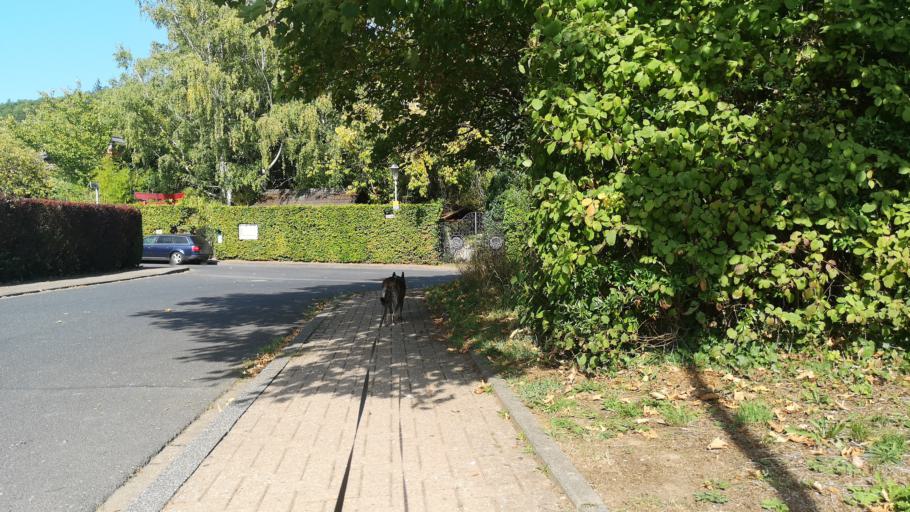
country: DE
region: North Rhine-Westphalia
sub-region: Regierungsbezirk Koln
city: Nideggen
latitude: 50.6727
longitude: 6.4757
